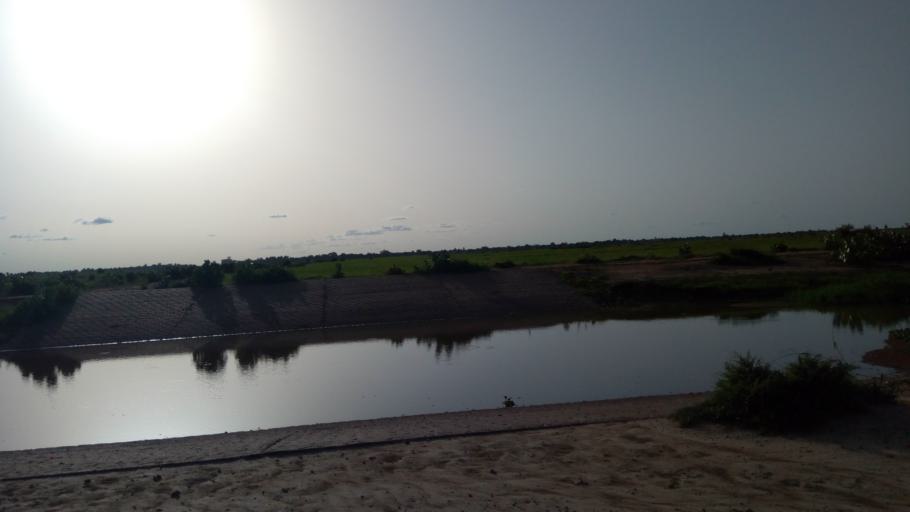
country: ML
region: Segou
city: Niono
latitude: 14.3049
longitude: -5.9397
